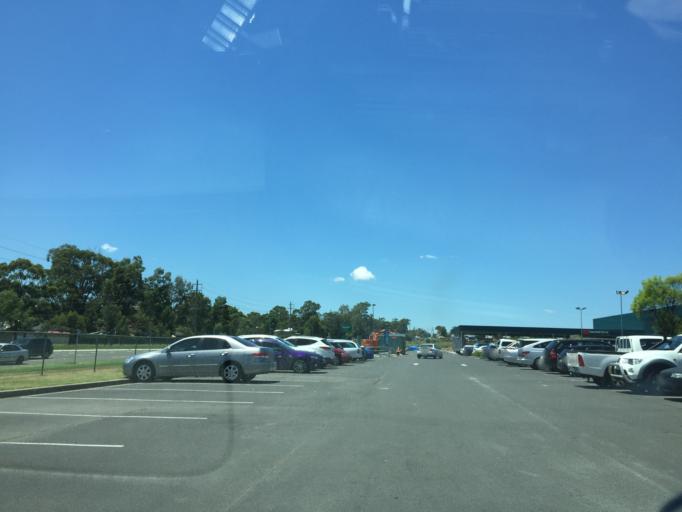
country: AU
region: New South Wales
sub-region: Blacktown
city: Mount Druitt
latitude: -33.7785
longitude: 150.8096
